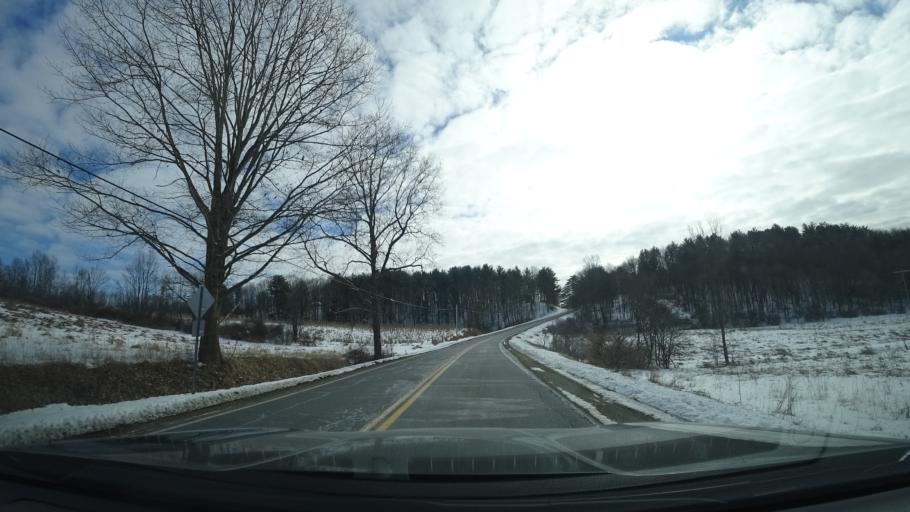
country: US
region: New York
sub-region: Washington County
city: Greenwich
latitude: 43.2432
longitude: -73.4071
